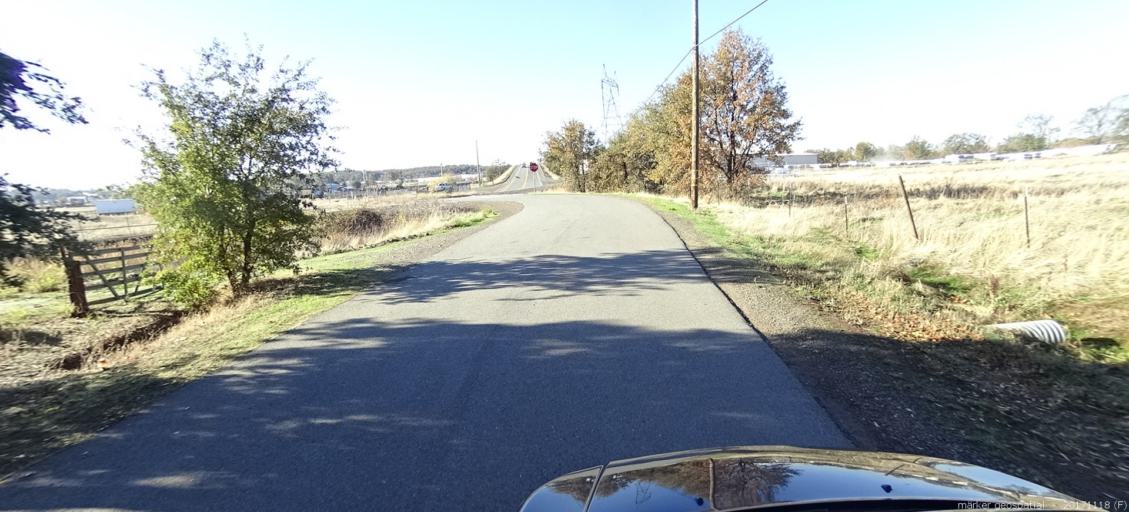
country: US
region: California
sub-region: Shasta County
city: Anderson
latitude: 40.4416
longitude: -122.2817
